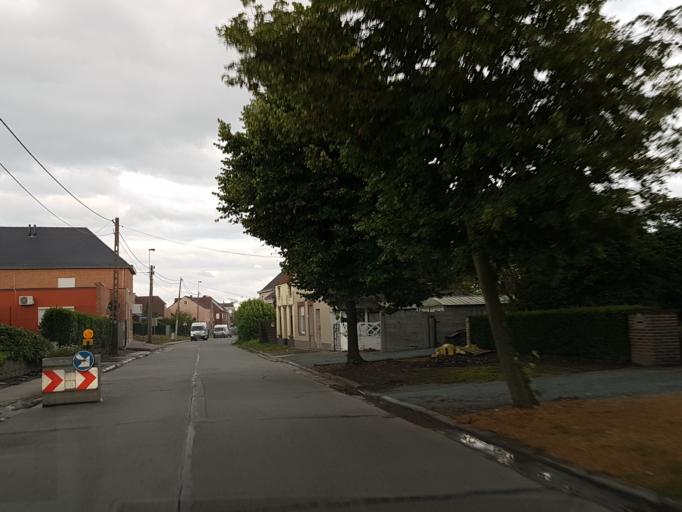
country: BE
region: Flanders
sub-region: Provincie Vlaams-Brabant
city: Opwijk
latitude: 50.9940
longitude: 4.1795
